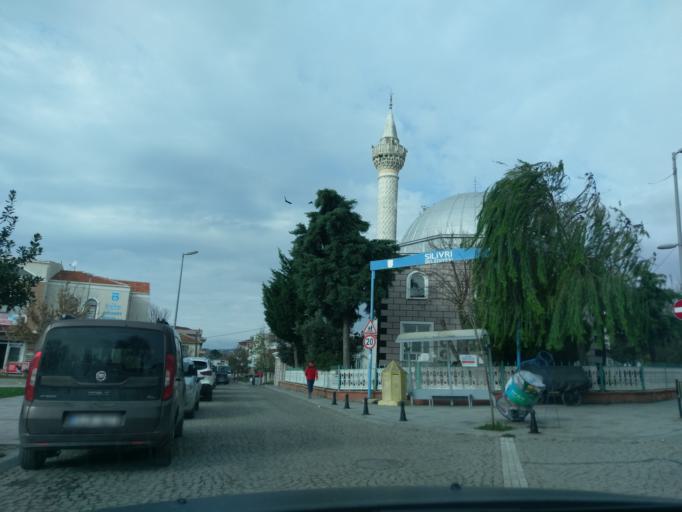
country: TR
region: Istanbul
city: Ortakoy
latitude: 41.1001
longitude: 28.3761
